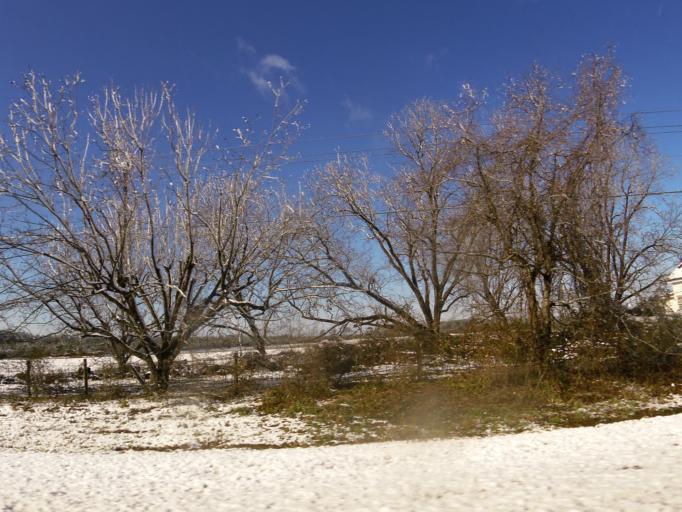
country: US
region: North Carolina
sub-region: Wilson County
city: Elm City
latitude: 35.7710
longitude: -77.8576
